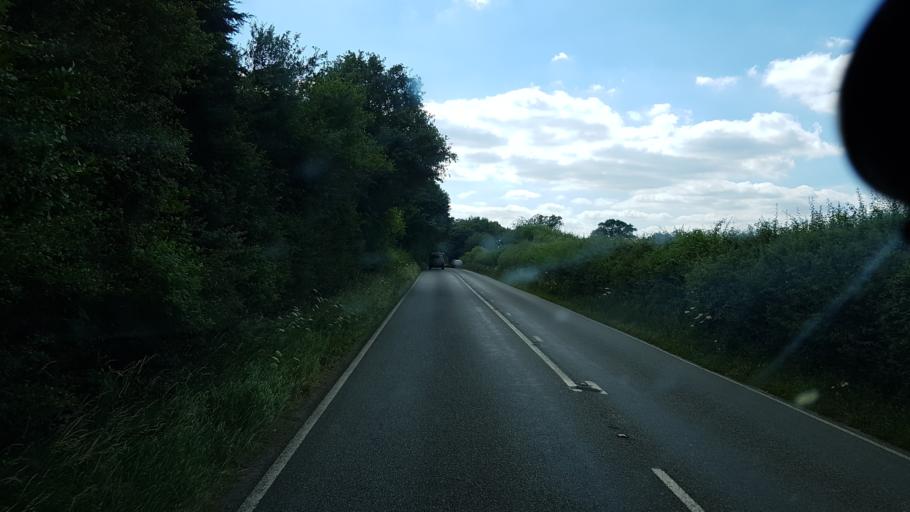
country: GB
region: England
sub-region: West Sussex
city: Southwater
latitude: 50.9942
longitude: -0.3963
